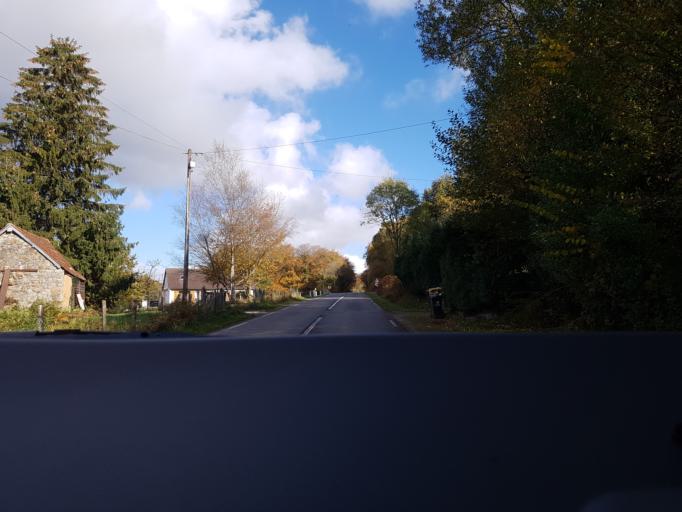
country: FR
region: Lower Normandy
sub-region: Departement de l'Orne
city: La Ferriere-aux-Etangs
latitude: 48.6573
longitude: -0.5255
